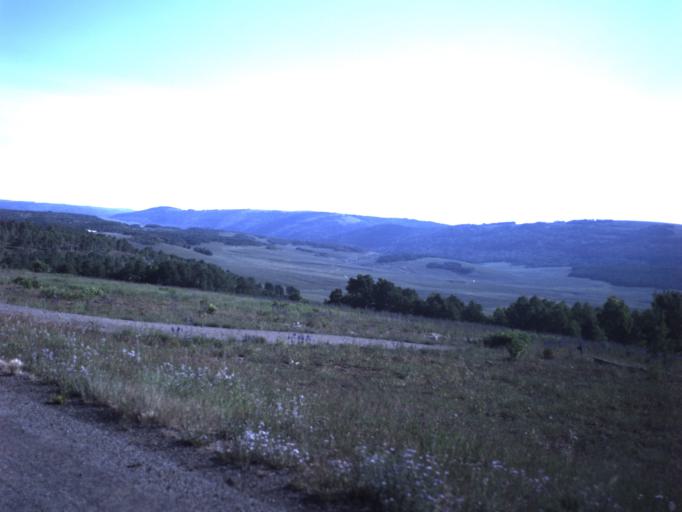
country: US
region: Utah
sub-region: Sanpete County
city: Fairview
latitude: 39.6499
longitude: -111.3286
